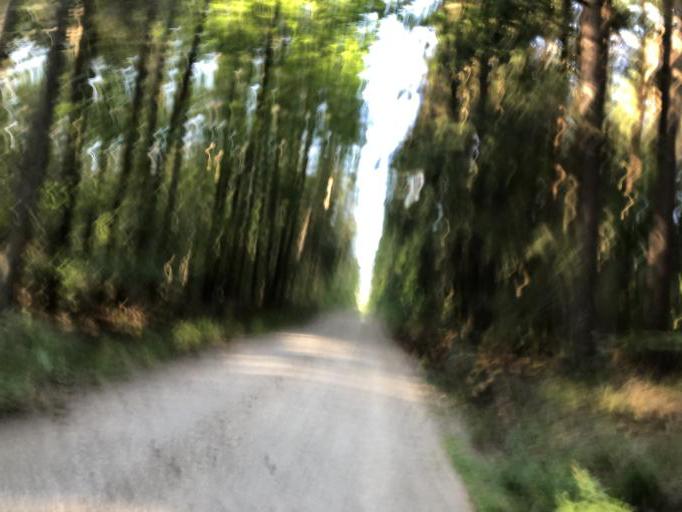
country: DE
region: Bavaria
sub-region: Regierungsbezirk Mittelfranken
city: Kalchreuth
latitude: 49.5493
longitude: 11.1005
